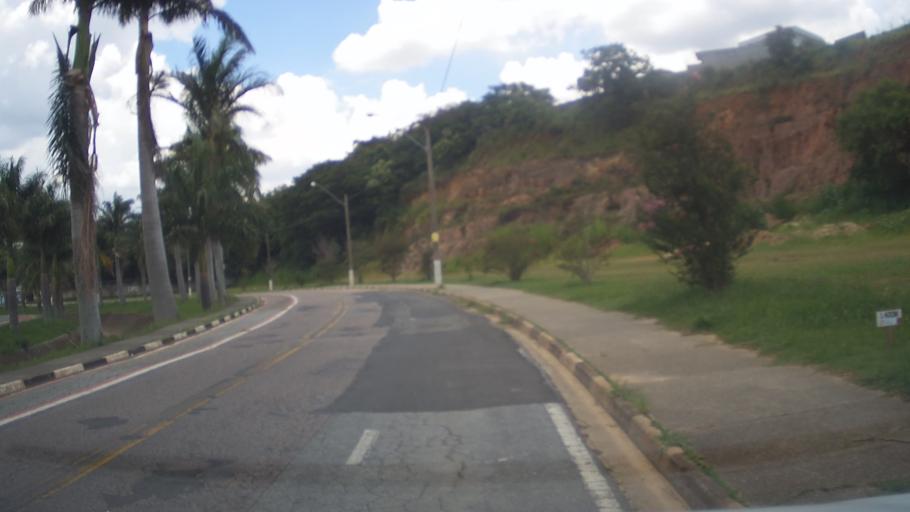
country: BR
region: Sao Paulo
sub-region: Vinhedo
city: Vinhedo
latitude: -23.0237
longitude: -46.9790
